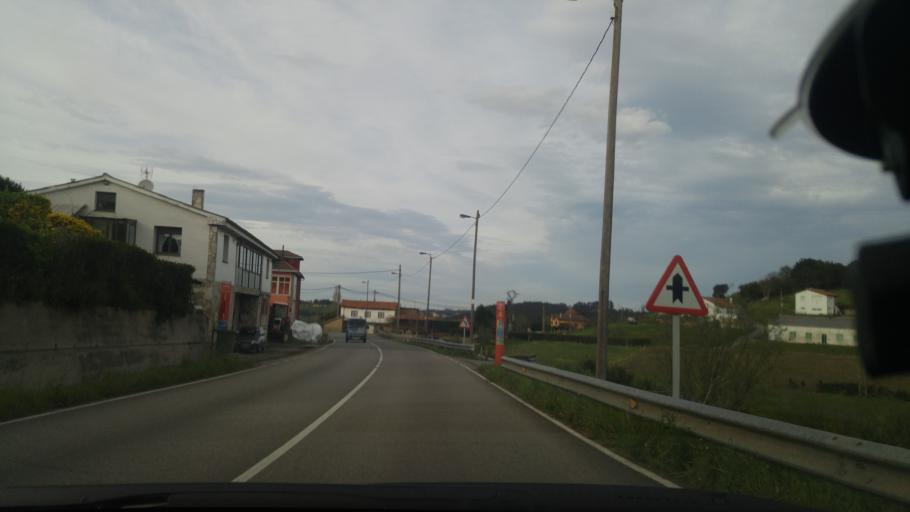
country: ES
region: Asturias
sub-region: Province of Asturias
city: Corvera de Asturias
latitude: 43.4751
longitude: -5.8447
